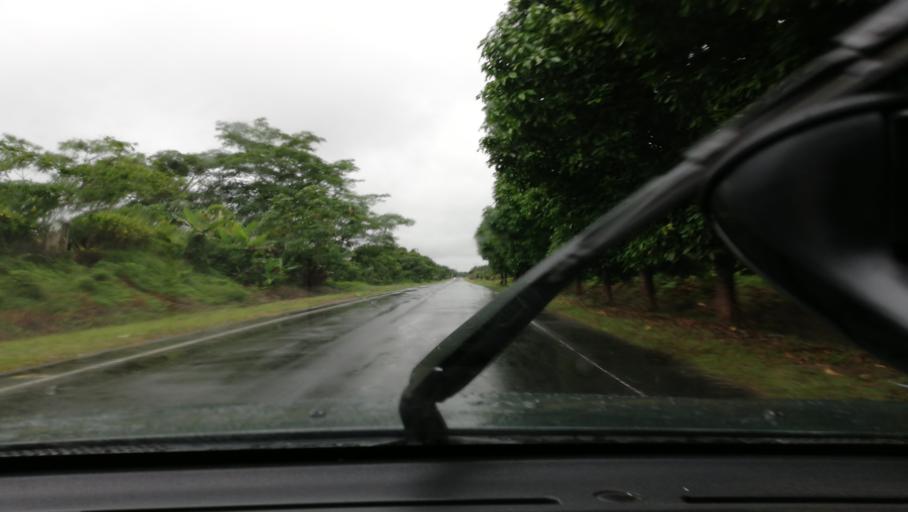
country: PE
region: Loreto
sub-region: Provincia de Maynas
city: San Juan
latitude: -4.0504
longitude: -73.4383
